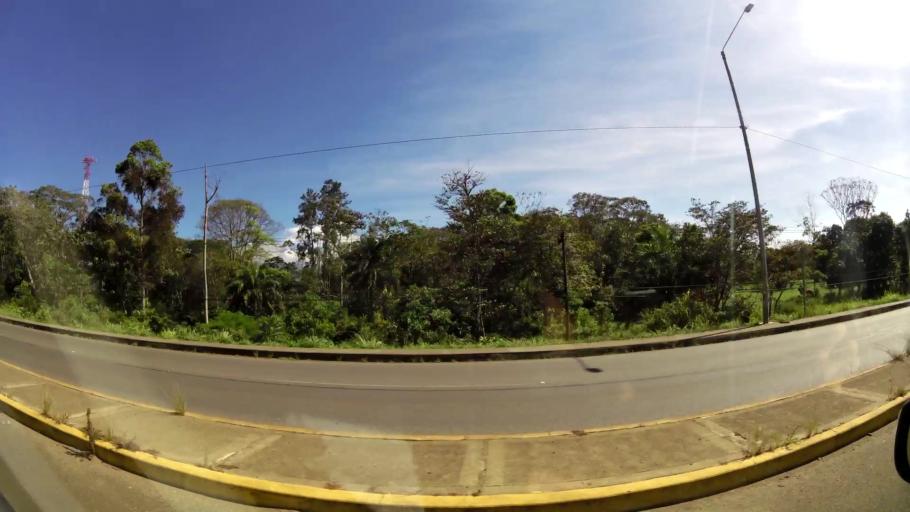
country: CR
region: San Jose
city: Daniel Flores
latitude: 9.3442
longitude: -83.6732
